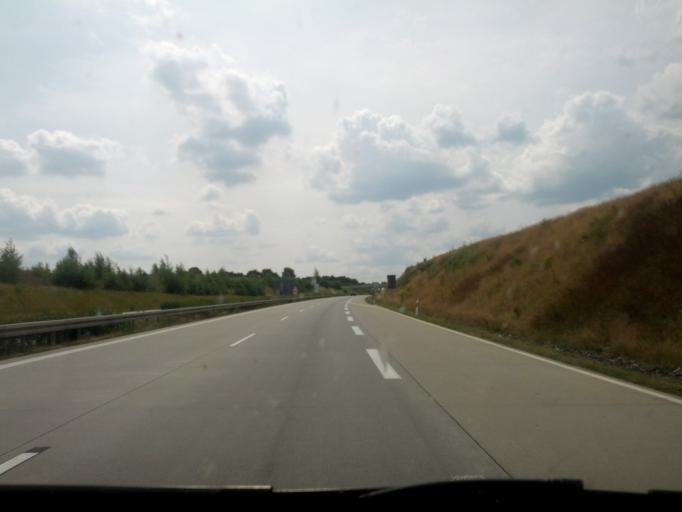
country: DE
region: Saxony
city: Liebstadt
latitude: 50.8956
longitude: 13.8897
